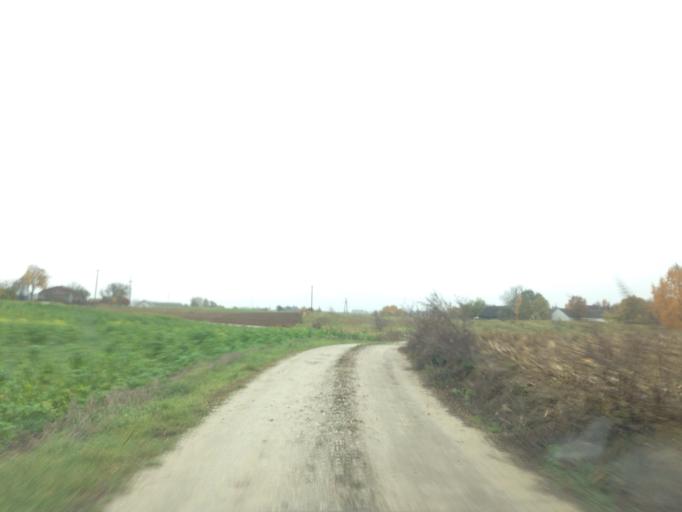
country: PL
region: Kujawsko-Pomorskie
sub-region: Powiat brodnicki
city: Bartniczka
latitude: 53.2138
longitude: 19.6060
